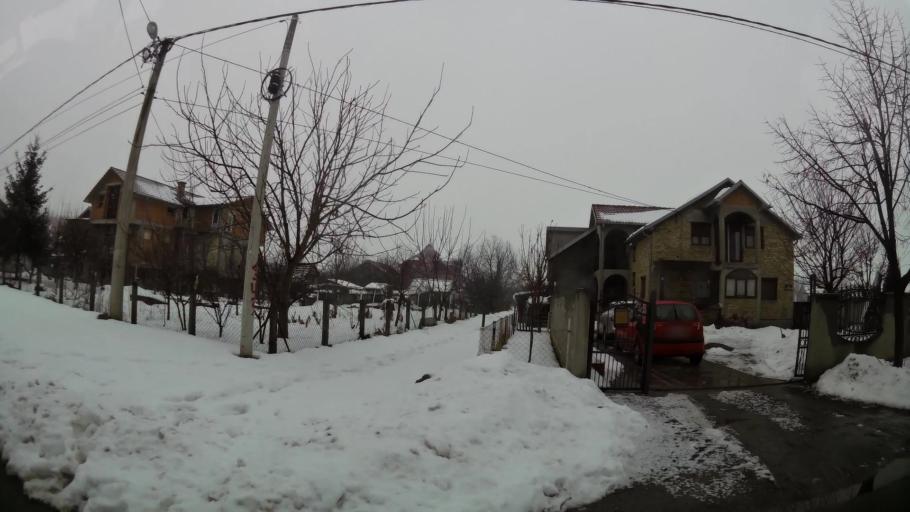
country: RS
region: Central Serbia
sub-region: Belgrade
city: Surcin
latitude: 44.8740
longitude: 20.3132
